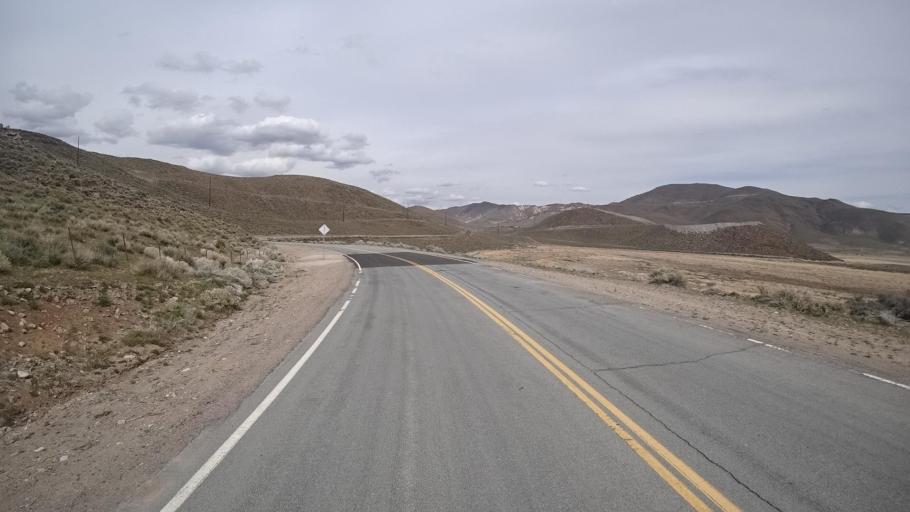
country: US
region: Nevada
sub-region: Washoe County
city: Sparks
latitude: 39.4609
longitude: -119.7412
